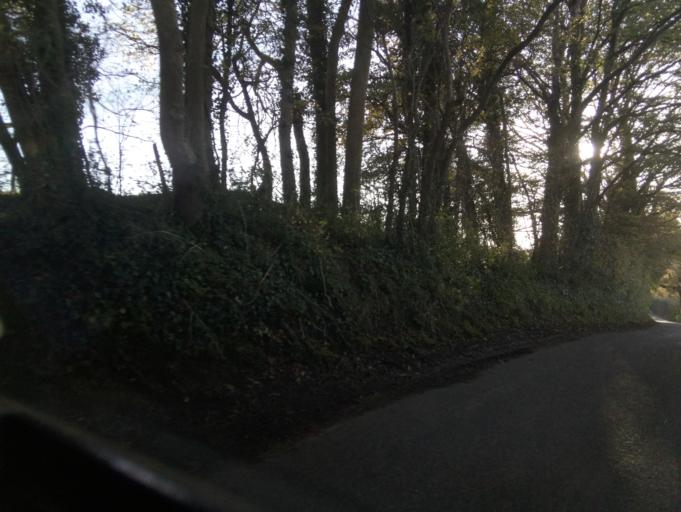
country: GB
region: England
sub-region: Somerset
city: Milborne Port
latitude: 50.9922
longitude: -2.4616
